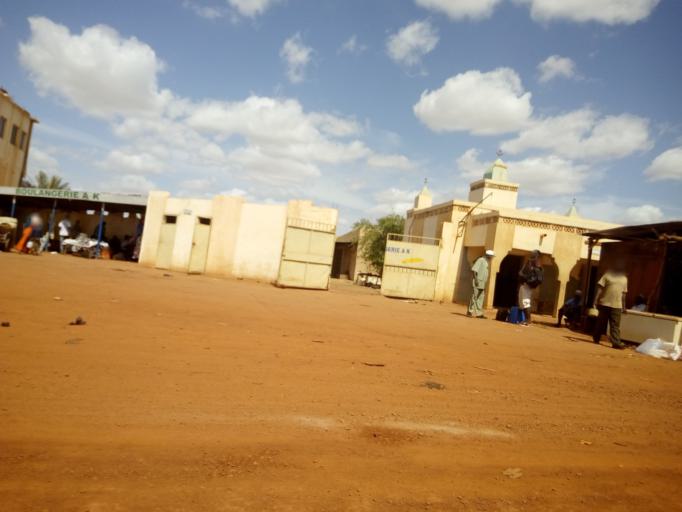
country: ML
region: Segou
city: Segou
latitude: 13.4396
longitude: -6.2366
